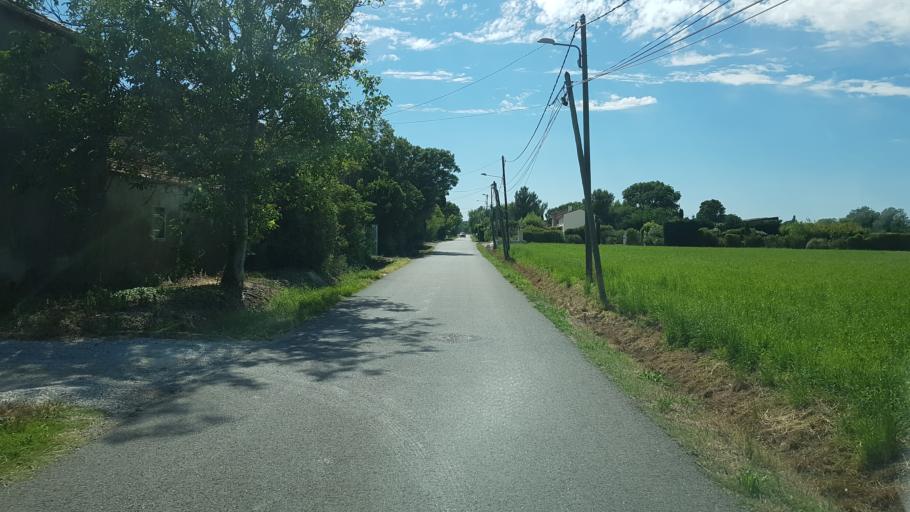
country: FR
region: Provence-Alpes-Cote d'Azur
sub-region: Departement des Bouches-du-Rhone
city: Saint-Martin-de-Crau
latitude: 43.6601
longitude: 4.7605
